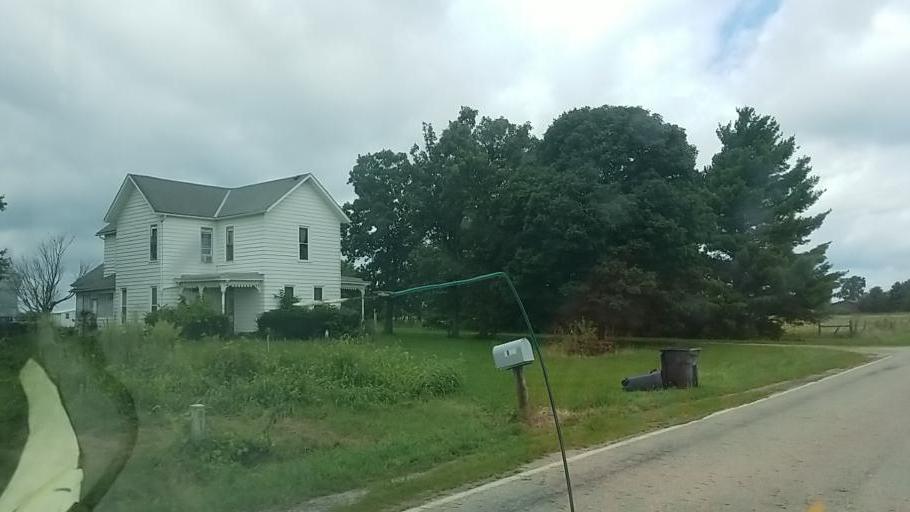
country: US
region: Ohio
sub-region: Madison County
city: Mount Sterling
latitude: 39.7888
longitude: -83.2276
